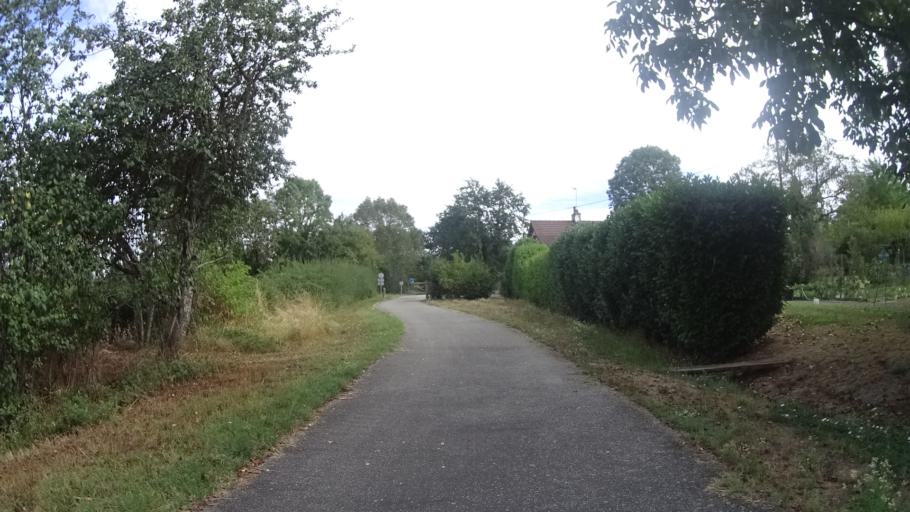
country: FR
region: Auvergne
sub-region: Departement de l'Allier
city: Diou
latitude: 46.5655
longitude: 3.7497
